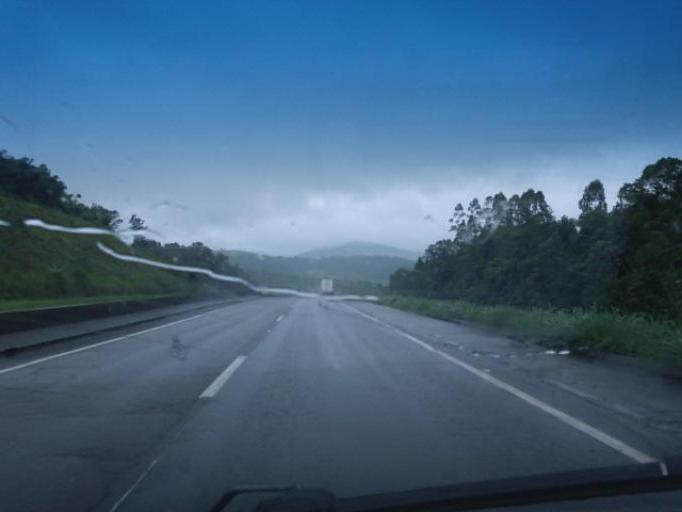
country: BR
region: Sao Paulo
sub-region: Cajati
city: Cajati
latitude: -24.7619
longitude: -48.1654
